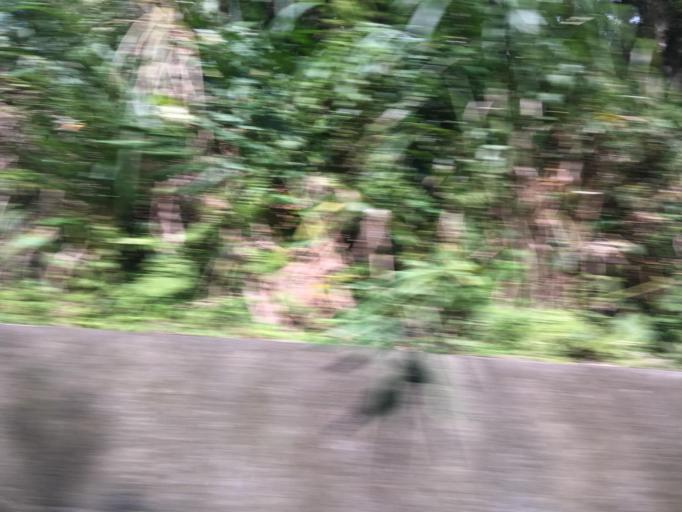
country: TW
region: Taiwan
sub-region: Yilan
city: Yilan
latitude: 24.7543
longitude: 121.6366
